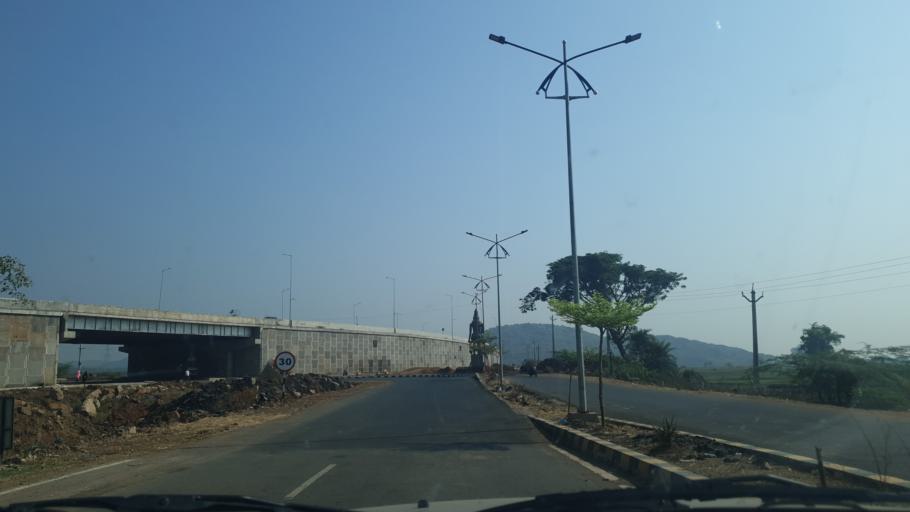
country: IN
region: Andhra Pradesh
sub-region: Srikakulam
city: Tekkali
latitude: 18.6181
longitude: 84.2426
